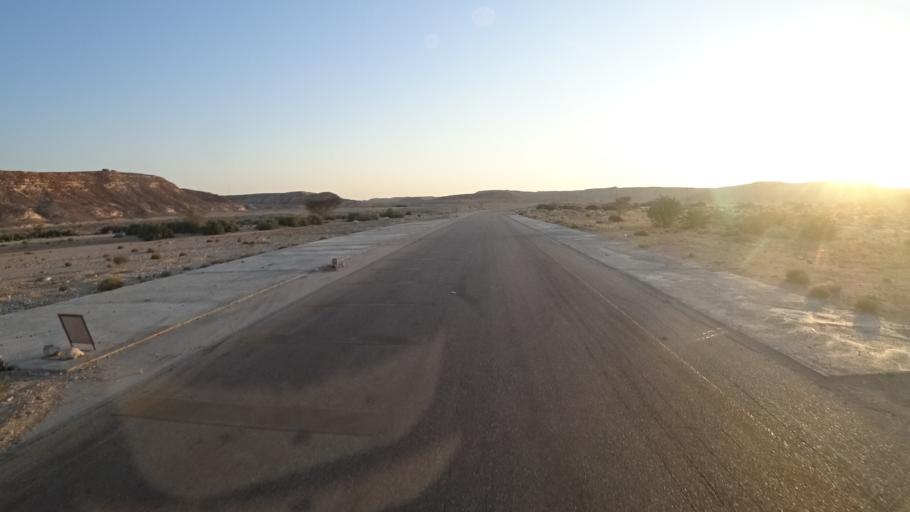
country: OM
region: Zufar
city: Salalah
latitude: 17.5132
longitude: 53.3718
